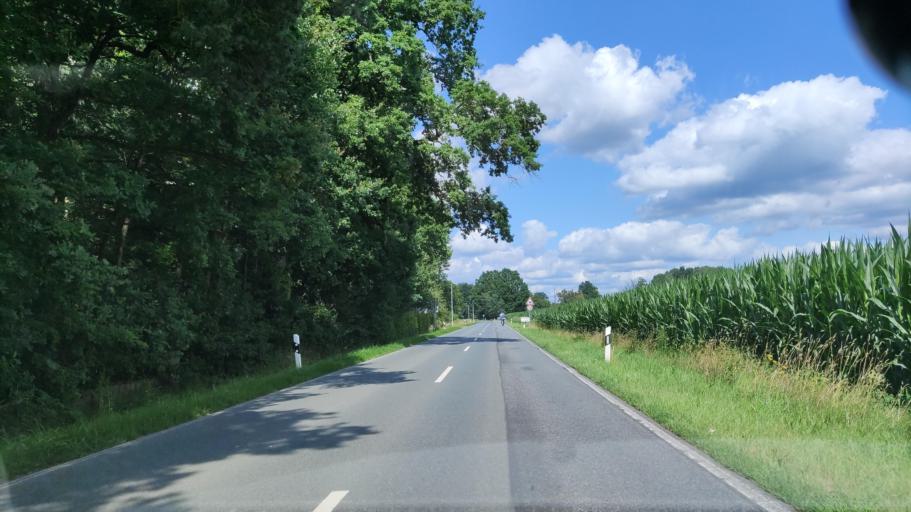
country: DE
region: Lower Saxony
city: Bad Fallingbostel
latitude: 52.9346
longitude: 9.7272
